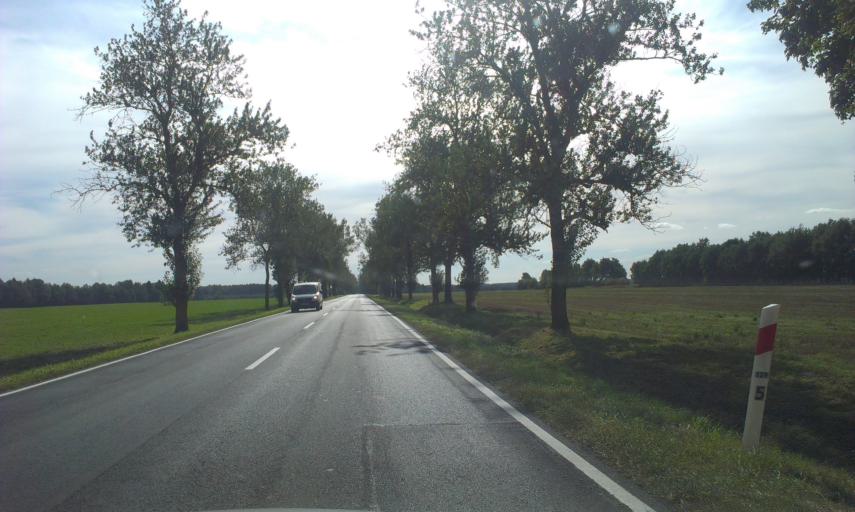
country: PL
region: Greater Poland Voivodeship
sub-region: Powiat zlotowski
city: Okonek
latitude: 53.5852
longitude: 16.8204
